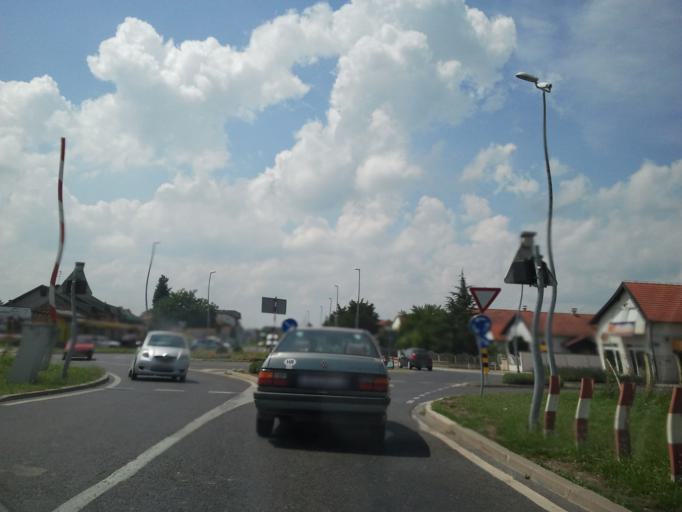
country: HR
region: Vukovarsko-Srijemska
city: Borovo
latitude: 45.3730
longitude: 18.9509
